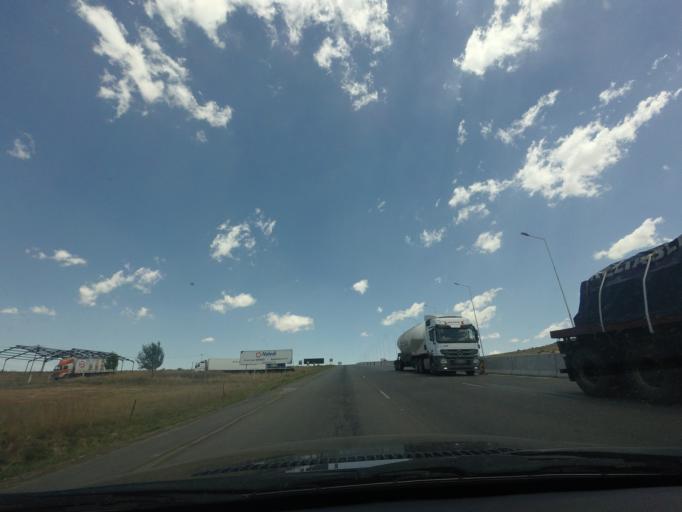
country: LS
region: Maseru
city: Maseru
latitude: -29.2959
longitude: 27.4440
